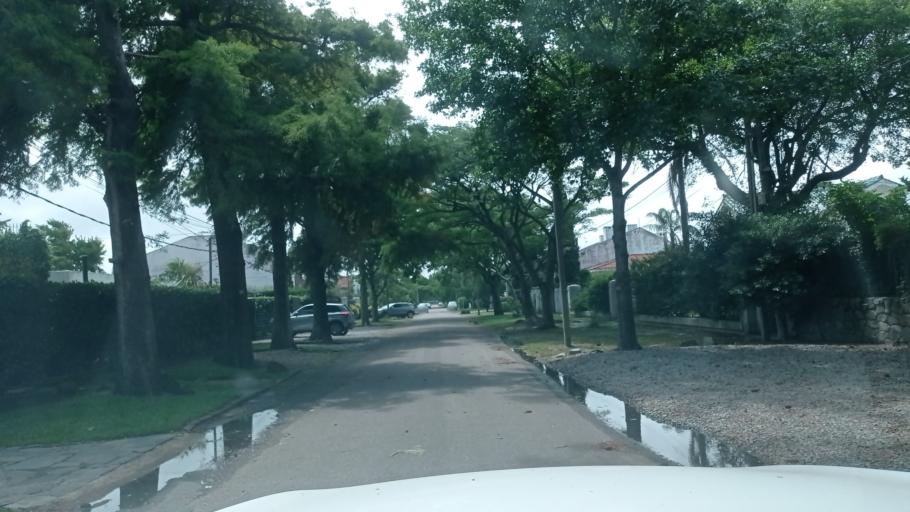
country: UY
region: Canelones
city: Barra de Carrasco
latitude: -34.8847
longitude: -56.0459
